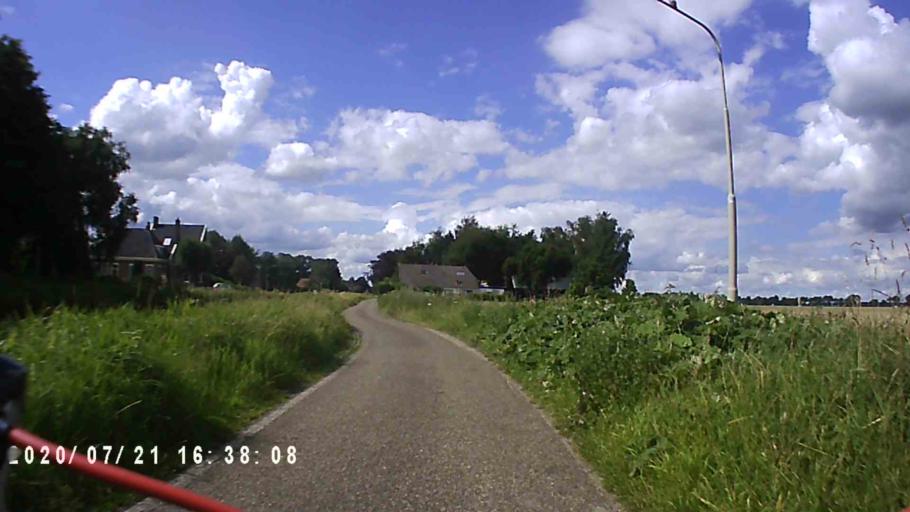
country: NL
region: Groningen
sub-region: Gemeente Hoogezand-Sappemeer
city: Sappemeer
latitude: 53.0916
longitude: 6.7950
